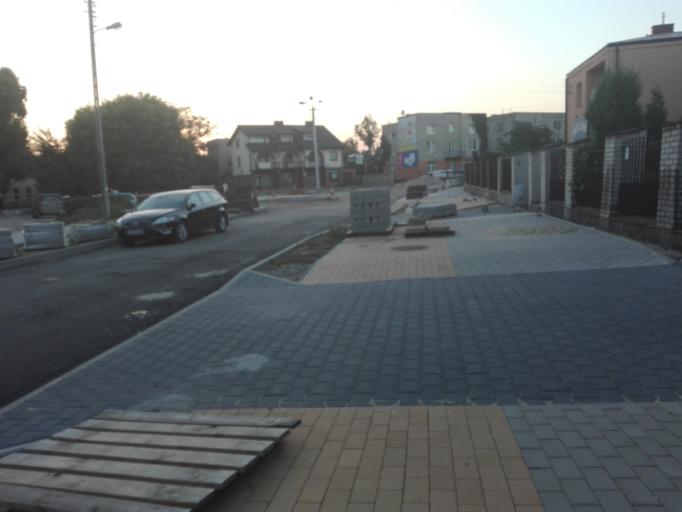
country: PL
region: Masovian Voivodeship
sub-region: Powiat sochaczewski
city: Sochaczew
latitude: 52.2216
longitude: 20.2365
